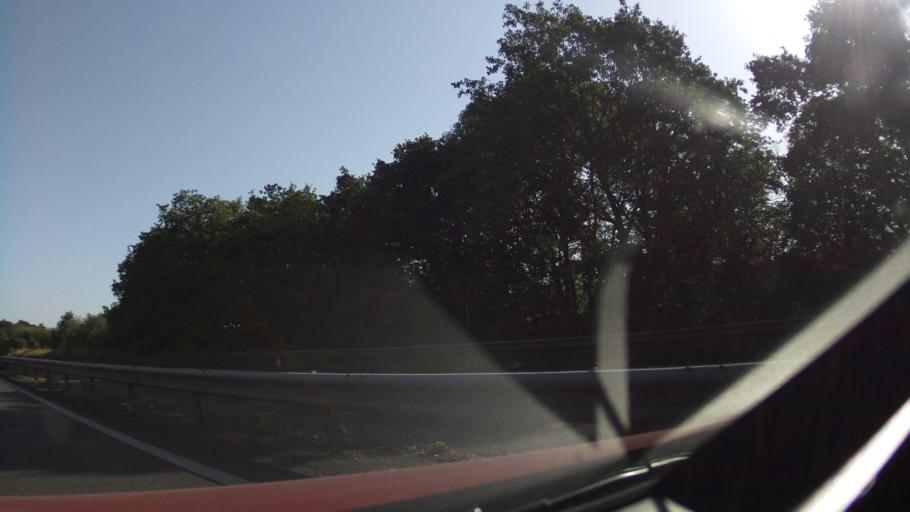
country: GB
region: England
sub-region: Warwickshire
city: Curdworth
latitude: 52.5599
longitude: -1.7710
